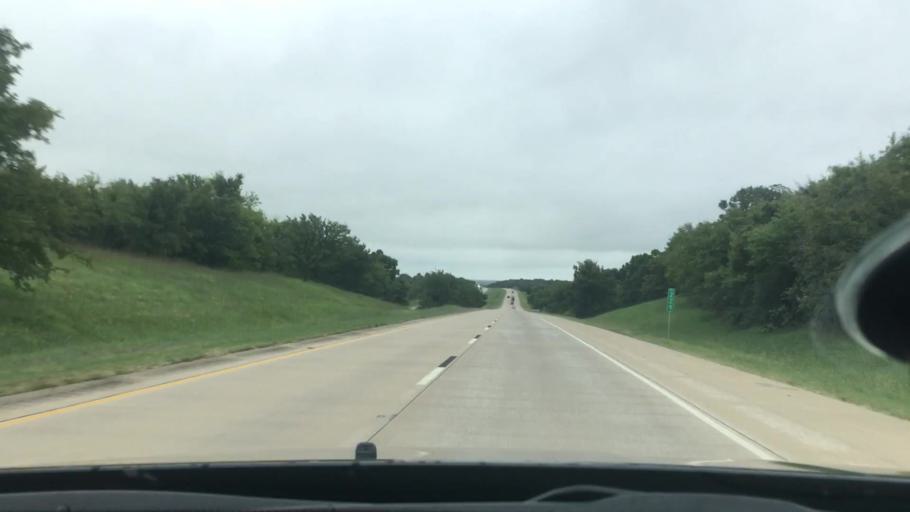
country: US
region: Oklahoma
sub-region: Okfuskee County
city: Okemah
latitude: 35.4280
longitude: -96.1733
